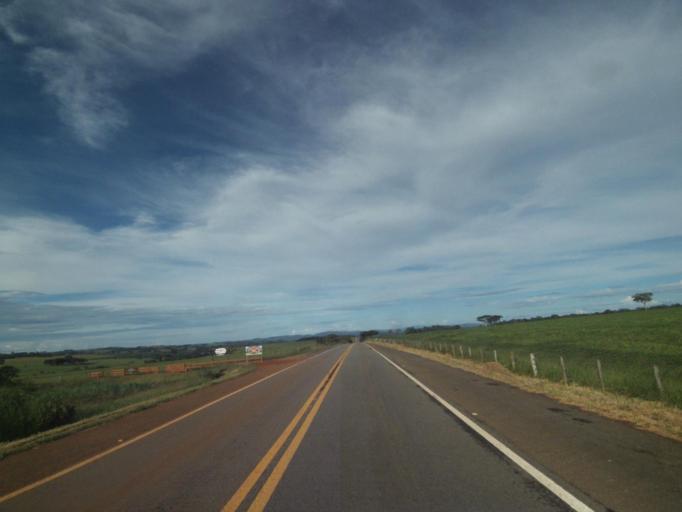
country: BR
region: Goias
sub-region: Itaberai
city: Itaberai
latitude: -15.9751
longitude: -49.6790
